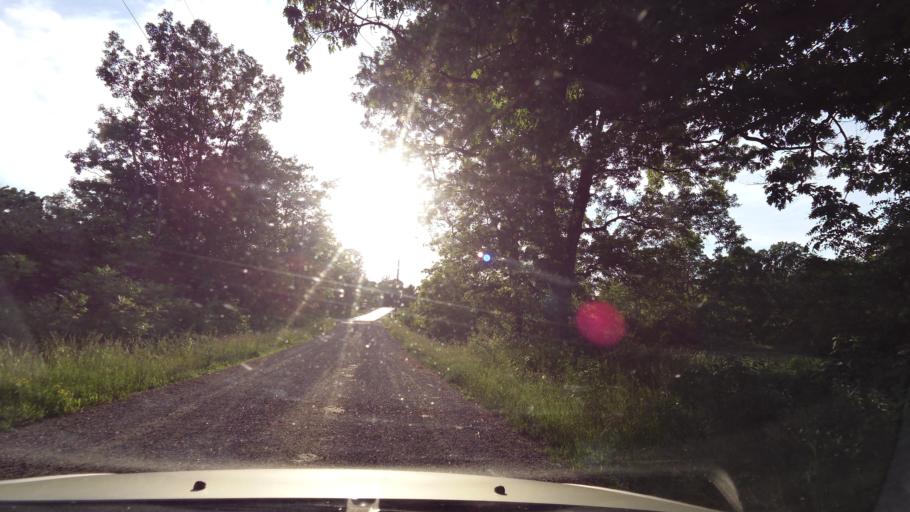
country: CA
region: Ontario
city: Ancaster
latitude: 43.0741
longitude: -79.9787
